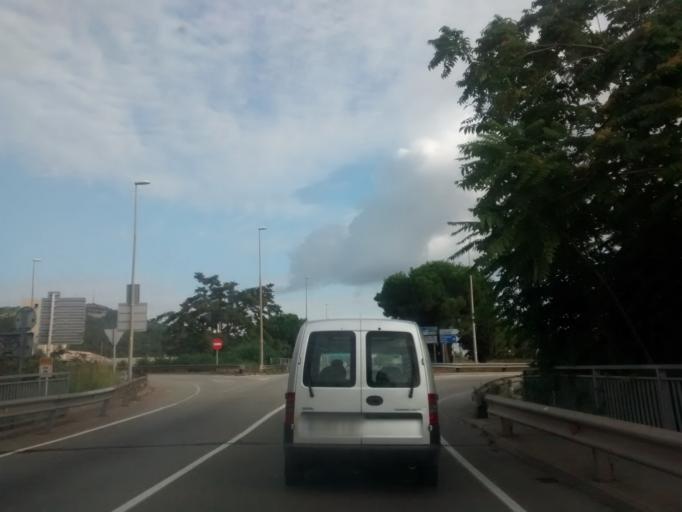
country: ES
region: Catalonia
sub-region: Provincia de Barcelona
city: Sant Vicenc dels Horts
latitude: 41.4044
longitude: 2.0053
